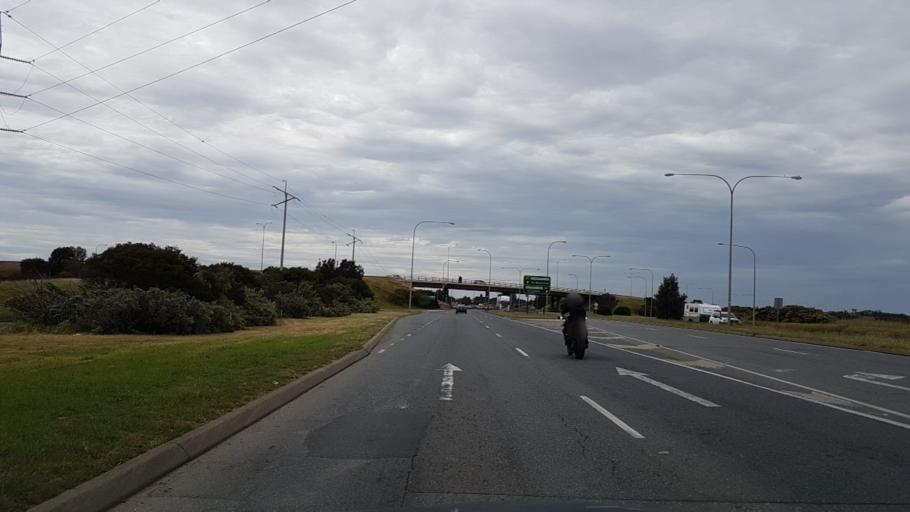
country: AU
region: South Australia
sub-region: Port Adelaide Enfield
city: Enfield
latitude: -34.8139
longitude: 138.5974
